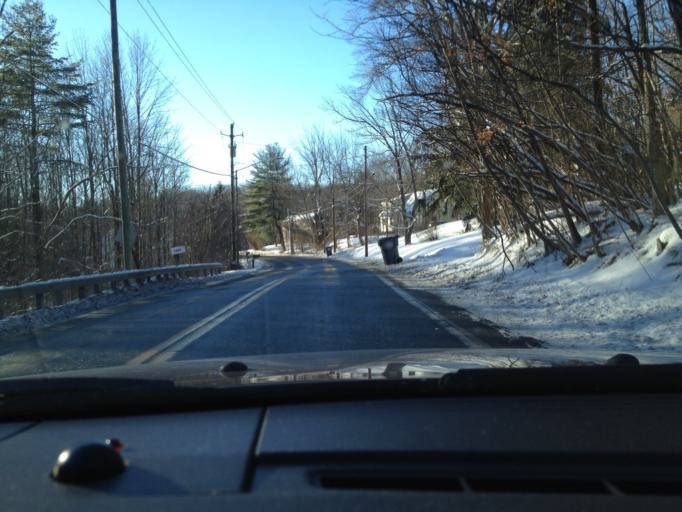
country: US
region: New York
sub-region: Rensselaer County
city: Averill Park
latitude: 42.6275
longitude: -73.5615
